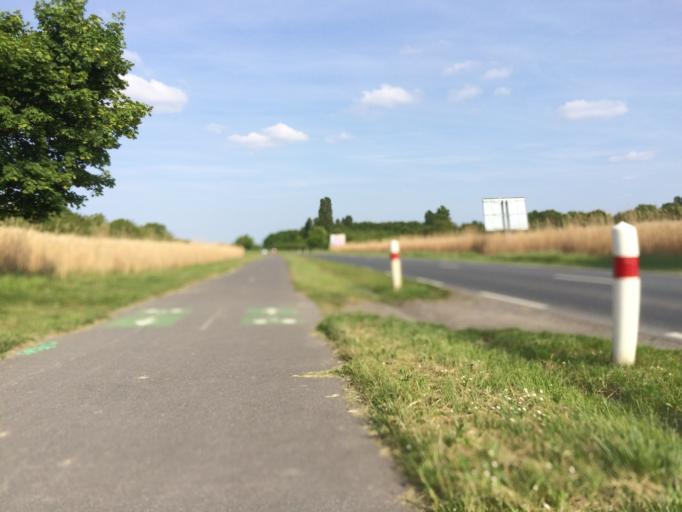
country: FR
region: Ile-de-France
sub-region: Departement de l'Essonne
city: Morangis
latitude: 48.7141
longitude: 2.3378
